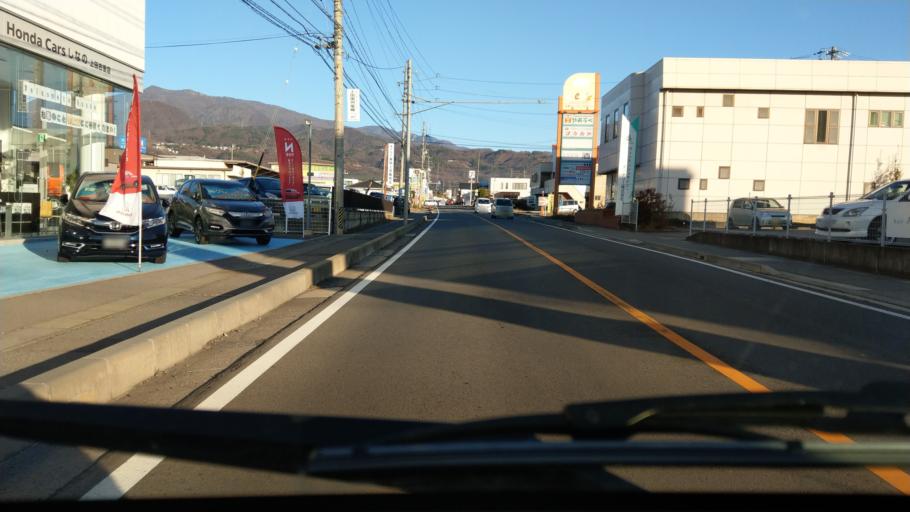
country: JP
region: Nagano
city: Ueda
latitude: 36.4015
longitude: 138.2842
